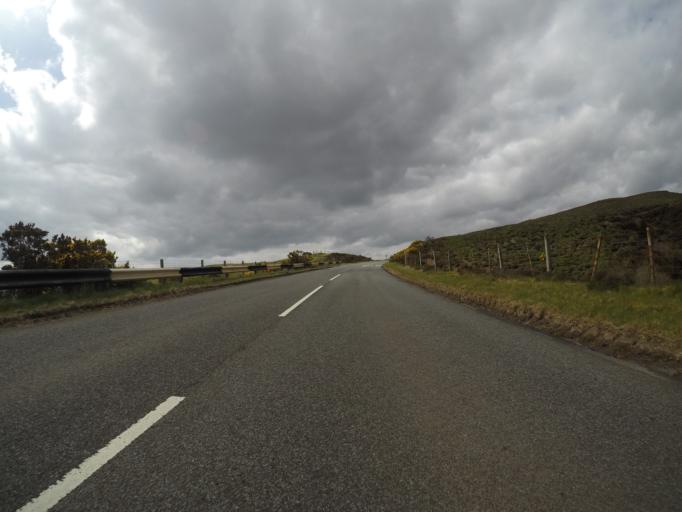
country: GB
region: Scotland
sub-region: Highland
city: Isle of Skye
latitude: 57.3054
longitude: -6.3128
